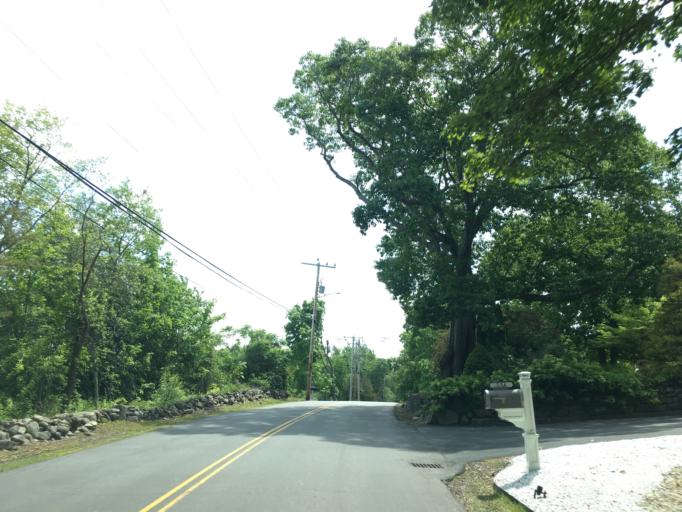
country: US
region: New Hampshire
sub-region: Rockingham County
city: Greenland
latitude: 43.0259
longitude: -70.8550
